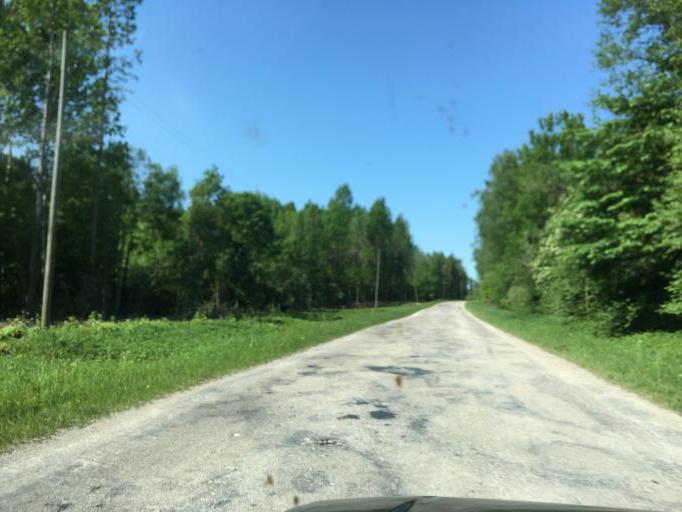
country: LV
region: Dundaga
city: Dundaga
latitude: 57.4527
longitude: 22.3215
